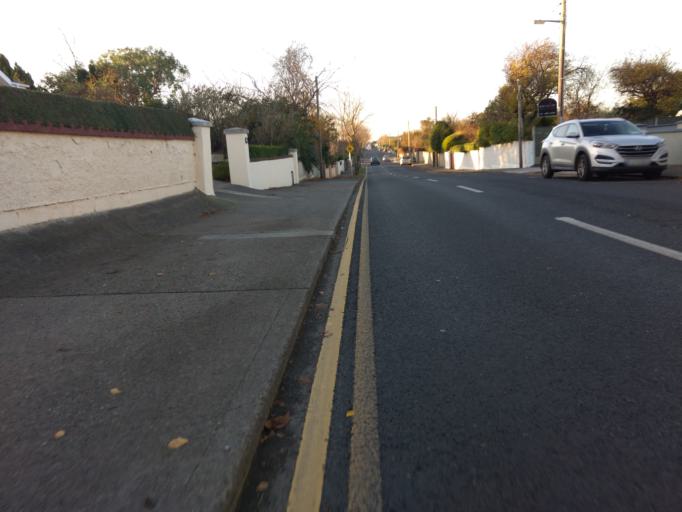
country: IE
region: Leinster
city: Malahide
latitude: 53.4507
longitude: -6.1678
